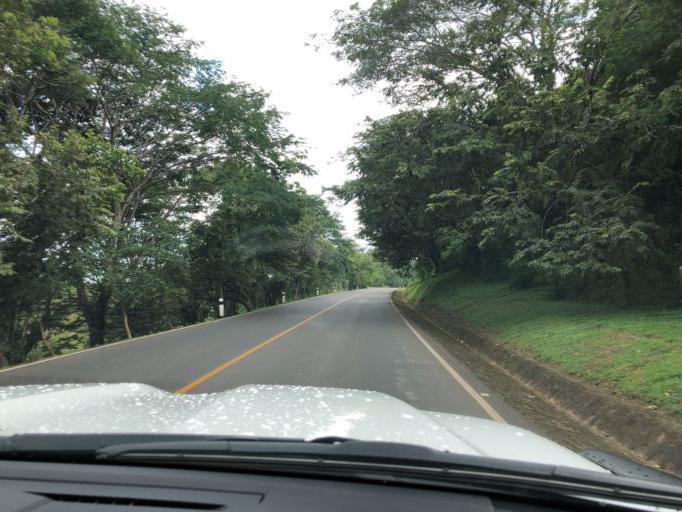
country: NI
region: Chontales
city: Villa Sandino
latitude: 11.9977
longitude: -84.8803
